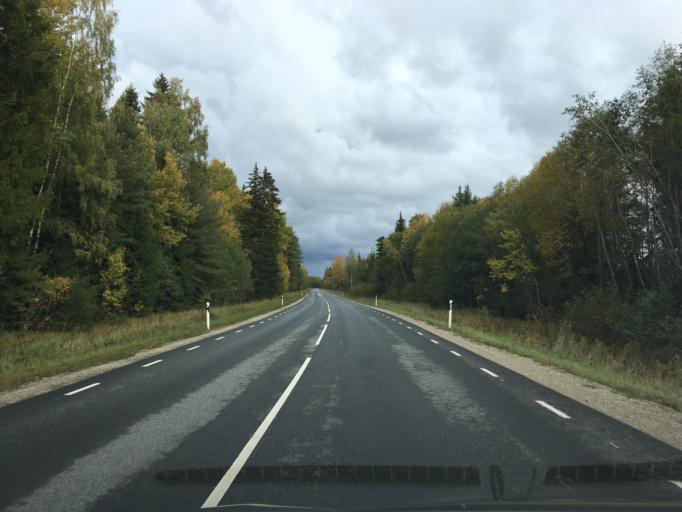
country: EE
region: Harju
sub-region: Anija vald
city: Kehra
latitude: 59.2636
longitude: 25.3526
